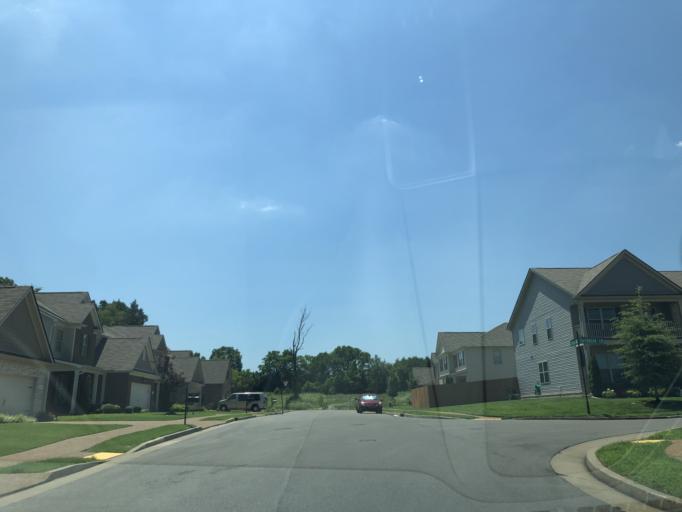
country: US
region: Tennessee
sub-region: Williamson County
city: Nolensville
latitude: 36.0191
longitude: -86.6676
